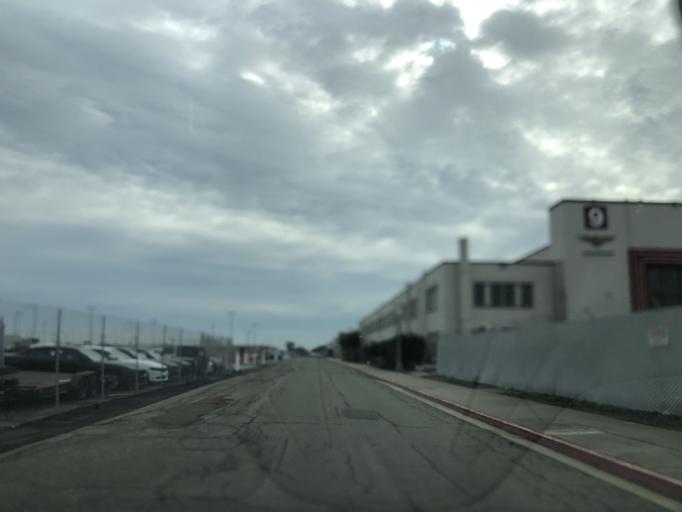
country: US
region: California
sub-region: Alameda County
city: Alameda
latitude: 37.7377
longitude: -122.2178
